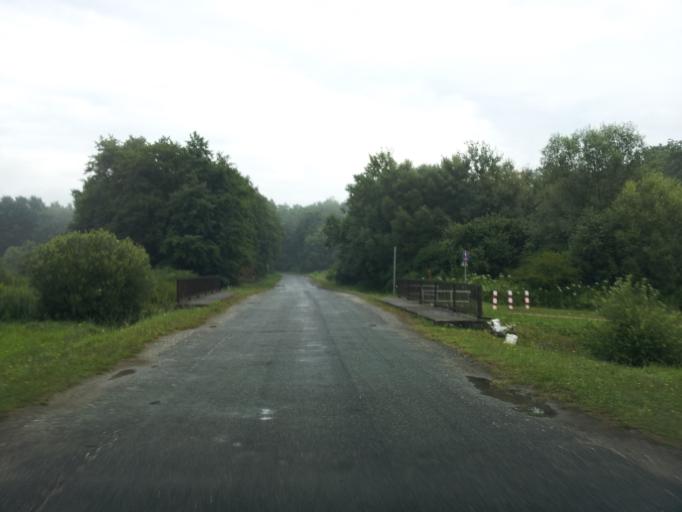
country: HU
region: Zala
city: Zalalovo
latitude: 46.8716
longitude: 16.5496
